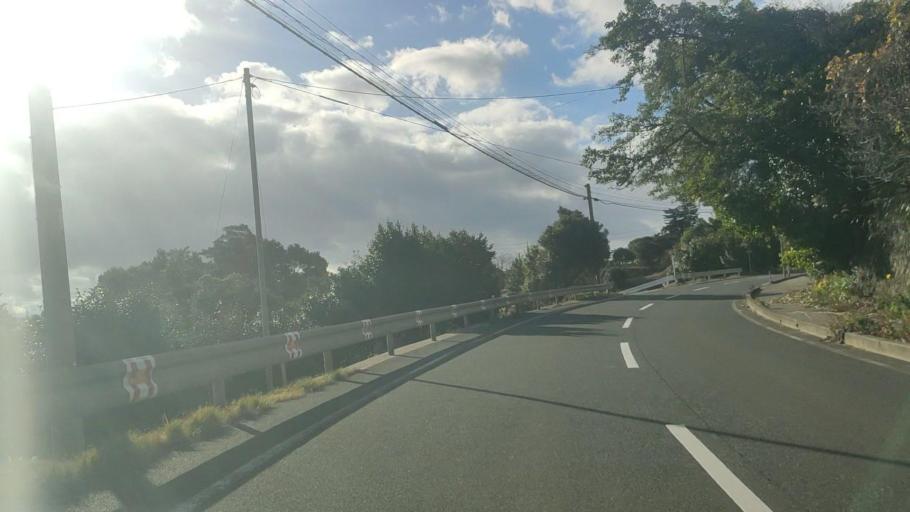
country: JP
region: Kagoshima
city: Hamanoichi
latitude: 31.6025
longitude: 130.7102
